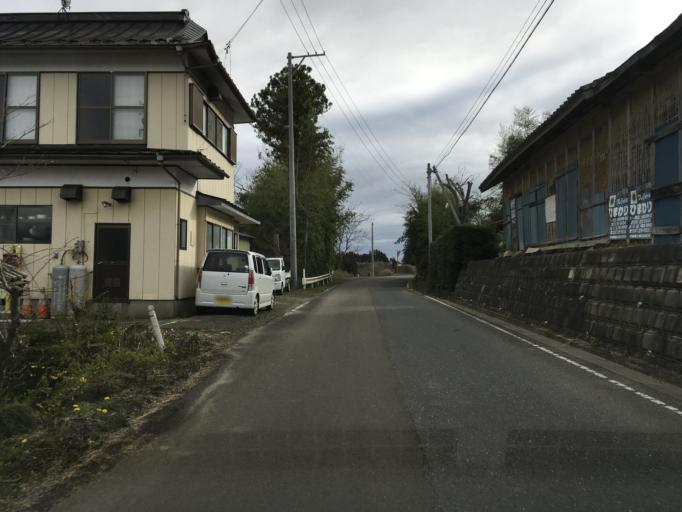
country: JP
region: Iwate
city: Ichinoseki
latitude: 38.7595
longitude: 141.2616
